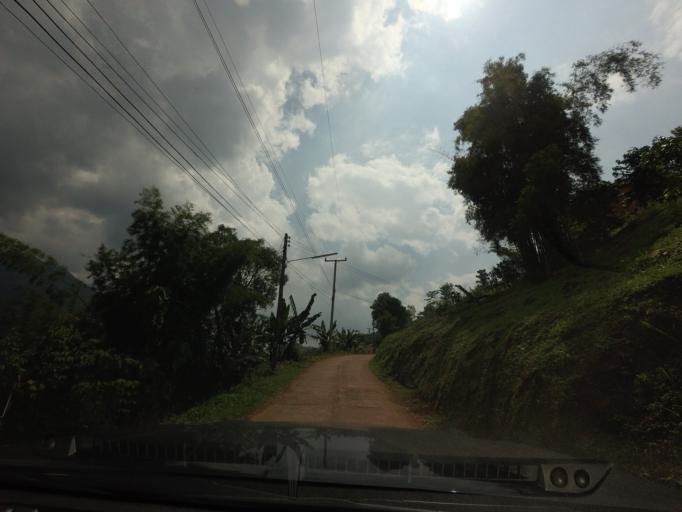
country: TH
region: Nan
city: Bo Kluea
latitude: 19.1899
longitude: 101.2006
